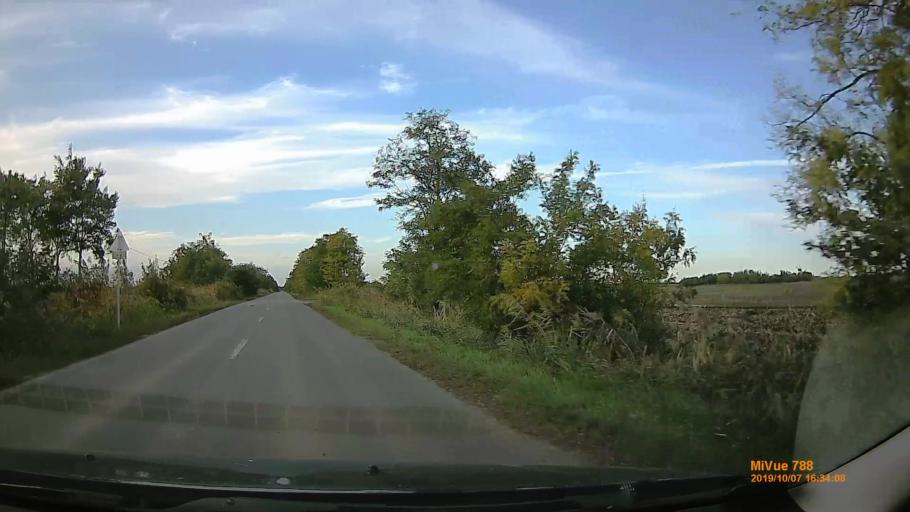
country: HU
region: Bekes
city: Szarvas
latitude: 46.7969
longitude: 20.6224
